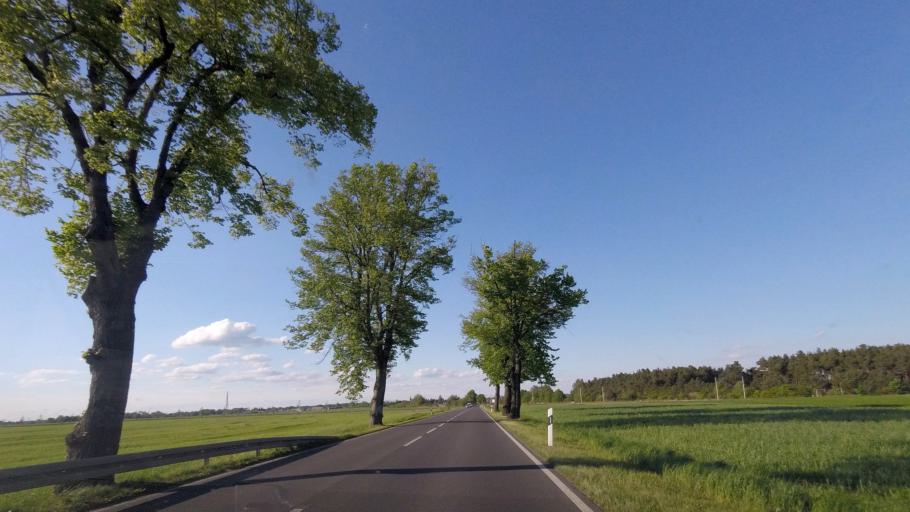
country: DE
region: Brandenburg
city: Luebben
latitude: 51.9162
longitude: 13.8951
